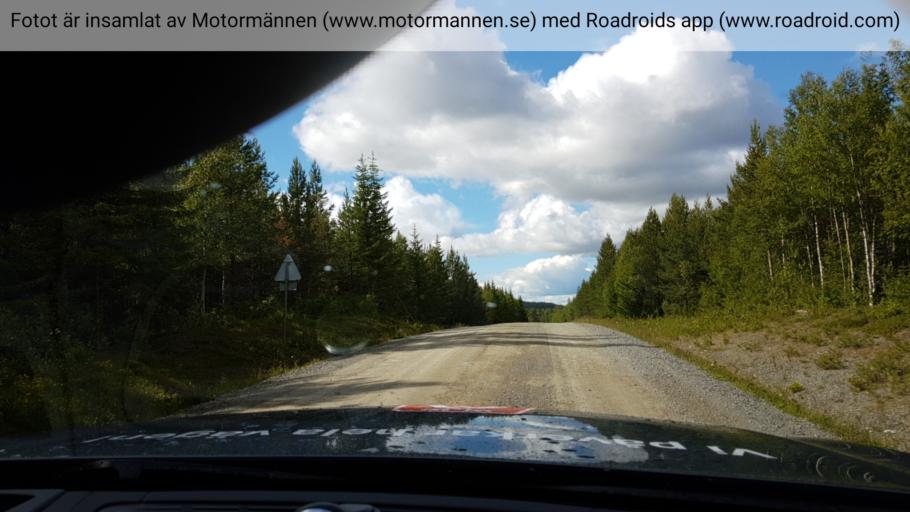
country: SE
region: Jaemtland
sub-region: Bergs Kommun
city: Hoverberg
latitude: 63.0240
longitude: 14.0808
